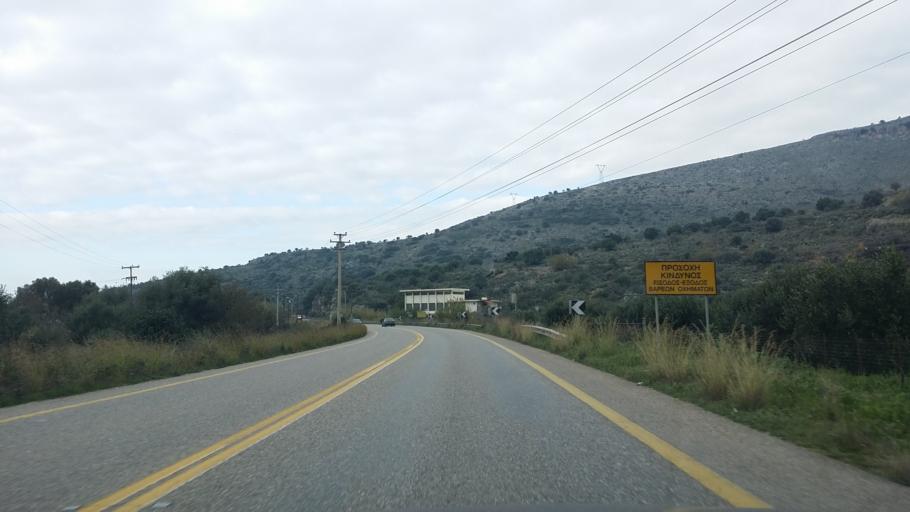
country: GR
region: West Greece
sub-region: Nomos Aitolias kai Akarnanias
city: Mesolongi
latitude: 38.4089
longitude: 21.4001
